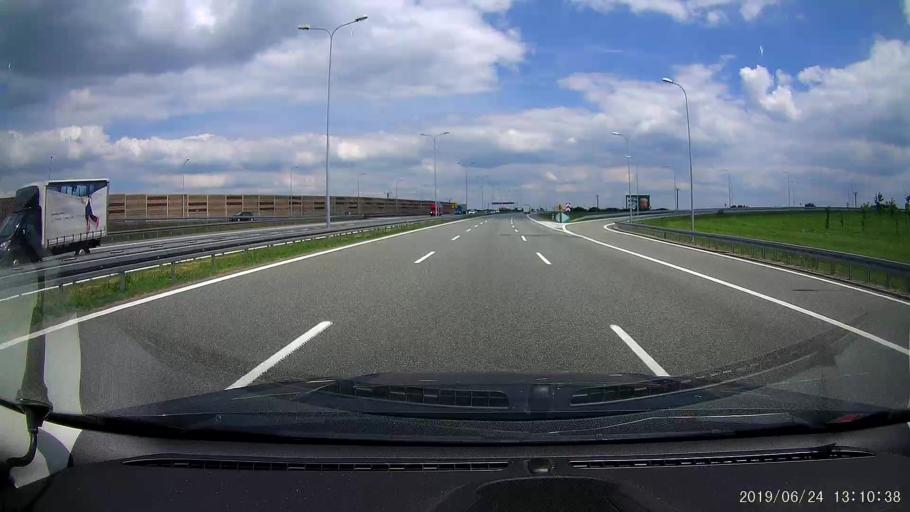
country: PL
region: Silesian Voivodeship
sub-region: Powiat gliwicki
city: Gieraltowice
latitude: 50.2251
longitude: 18.6942
